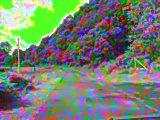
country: IE
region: Ulster
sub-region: County Donegal
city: Dunlewy
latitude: 54.9176
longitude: -8.1895
